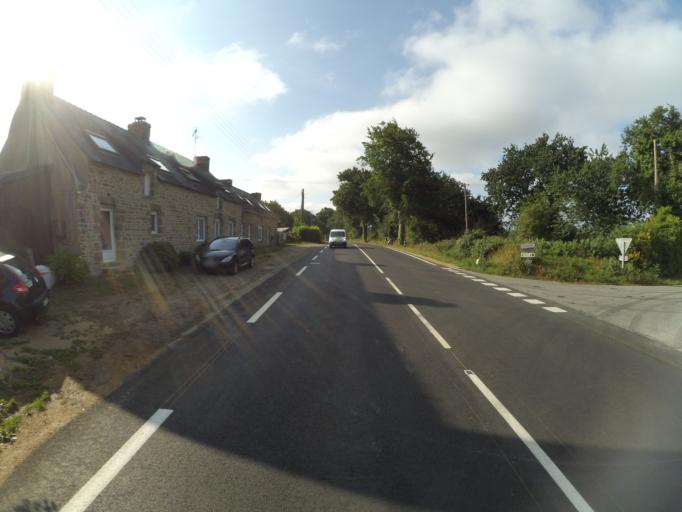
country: FR
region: Brittany
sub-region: Departement du Finistere
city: Redene
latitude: 47.8316
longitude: -3.4994
